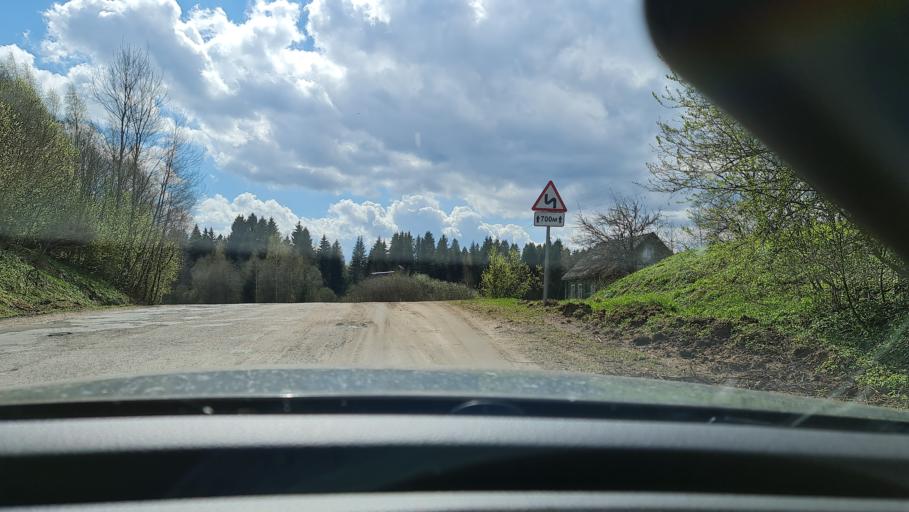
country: RU
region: Tverskaya
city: Toropets
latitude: 56.6419
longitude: 31.4218
